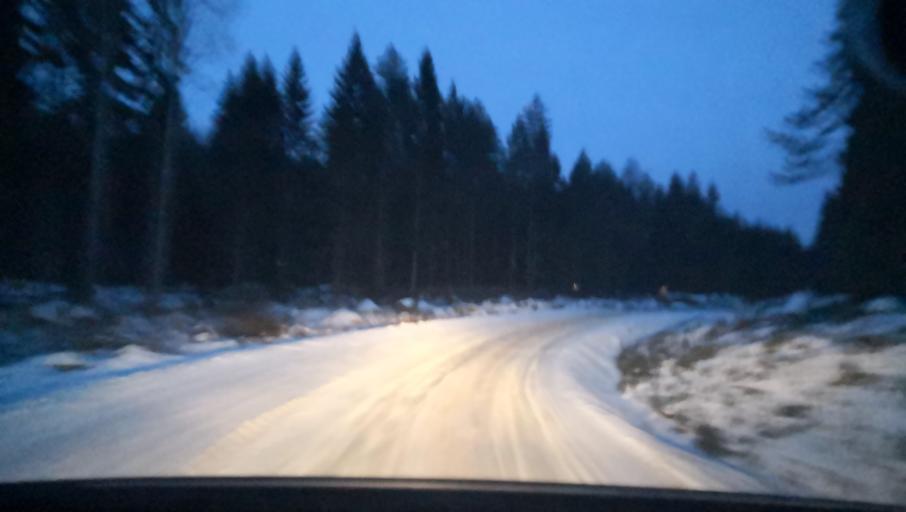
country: SE
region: Uppsala
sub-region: Heby Kommun
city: Tarnsjo
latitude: 60.2423
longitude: 16.7064
